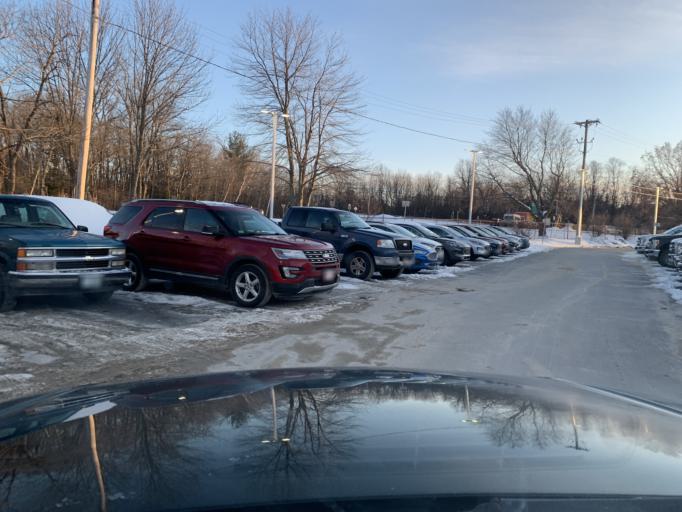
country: US
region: Massachusetts
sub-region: Essex County
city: Haverhill
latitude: 42.7851
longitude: -71.1174
